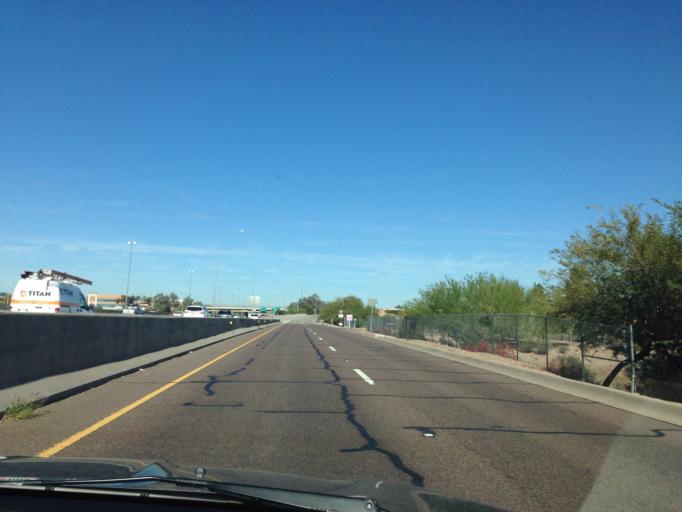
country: US
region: Arizona
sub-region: Maricopa County
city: Glendale
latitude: 33.6576
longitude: -112.1139
